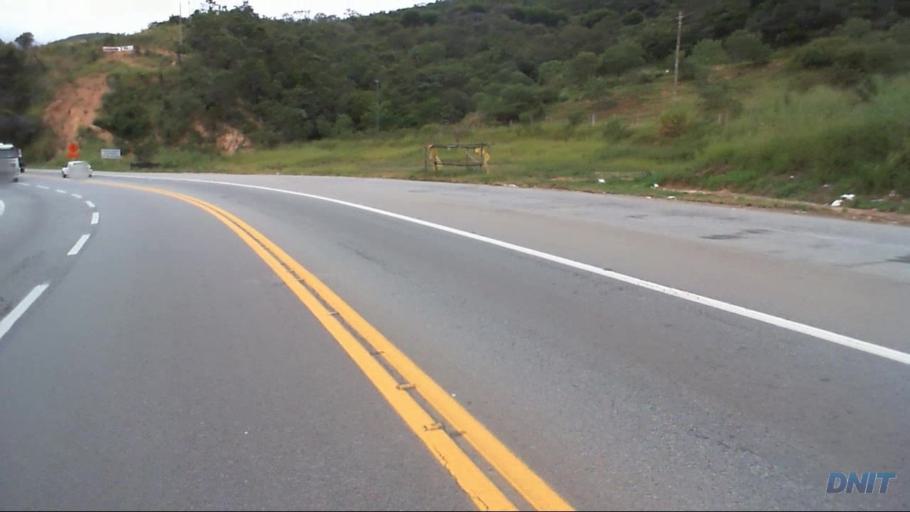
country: BR
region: Minas Gerais
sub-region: Caete
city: Caete
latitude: -19.7956
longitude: -43.6774
